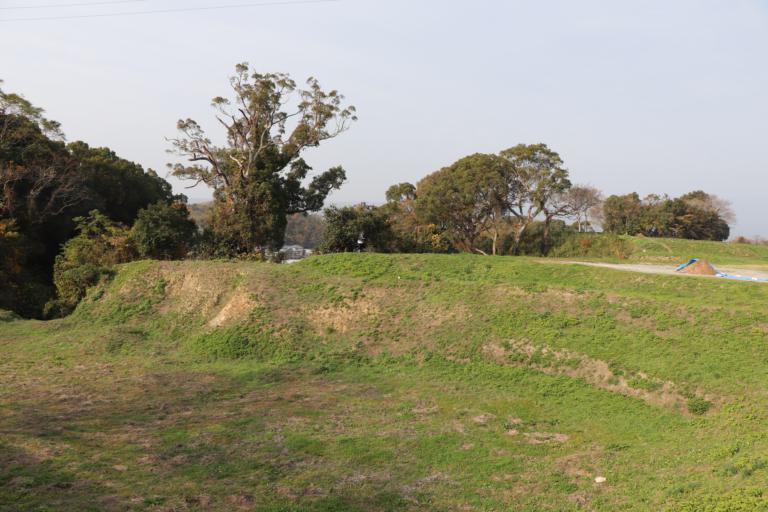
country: JP
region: Kumamoto
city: Hondo
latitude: 32.6302
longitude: 130.2540
